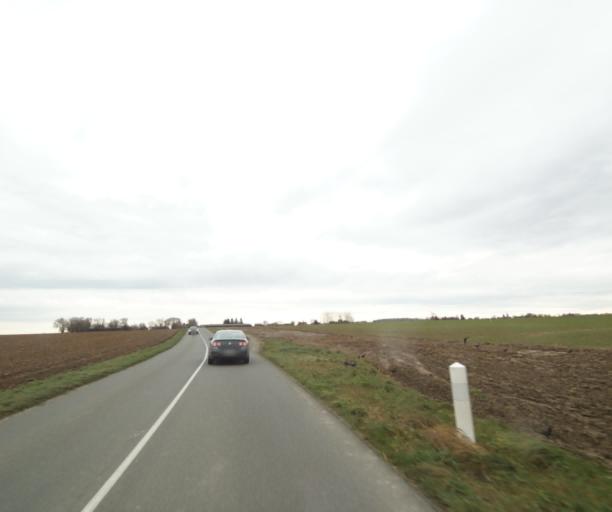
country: FR
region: Nord-Pas-de-Calais
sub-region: Departement du Nord
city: Sebourg
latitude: 50.3514
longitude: 3.6283
